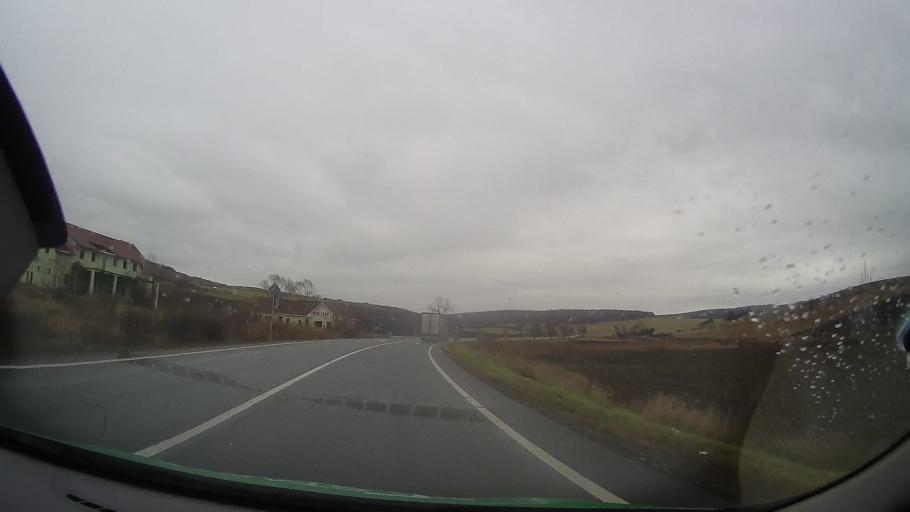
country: RO
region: Mures
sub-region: Comuna Lunca
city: Lunca
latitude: 46.8696
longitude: 24.5530
